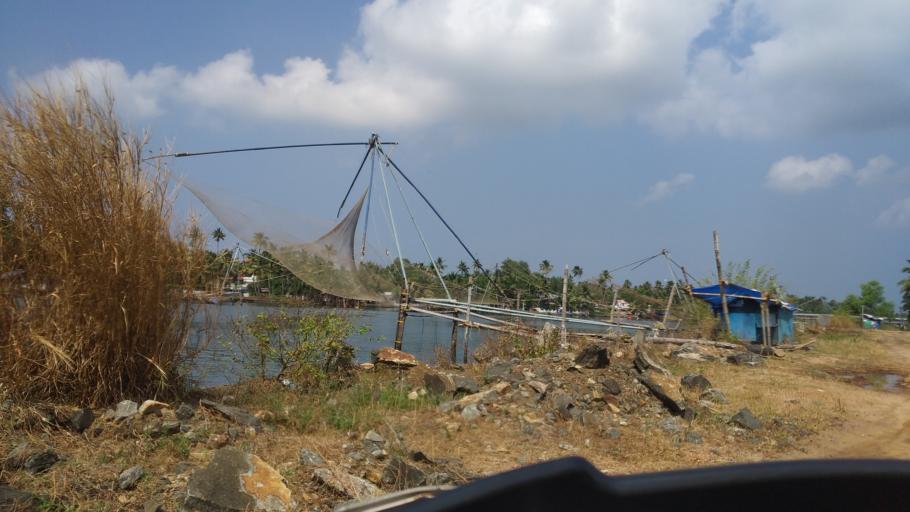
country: IN
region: Kerala
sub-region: Thrissur District
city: Kodungallur
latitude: 10.1373
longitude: 76.2051
